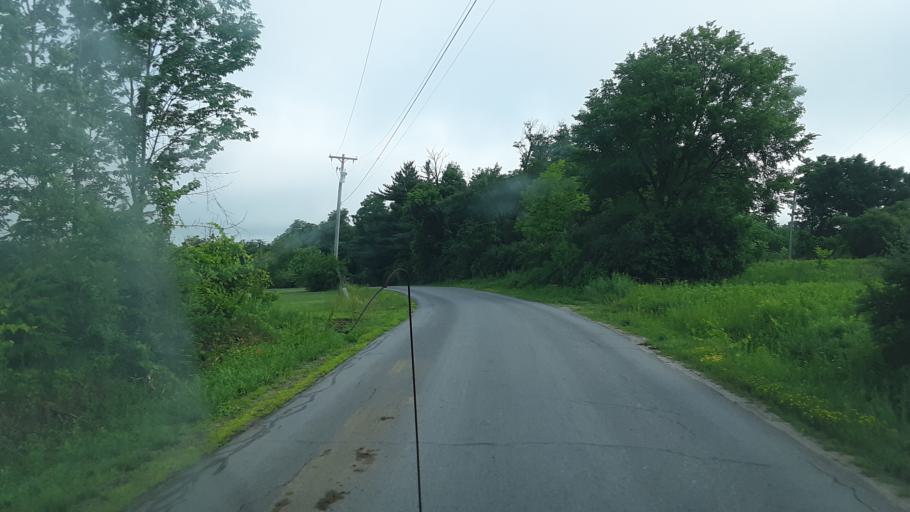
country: US
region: New York
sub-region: Montgomery County
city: Fonda
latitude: 42.8749
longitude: -74.3768
